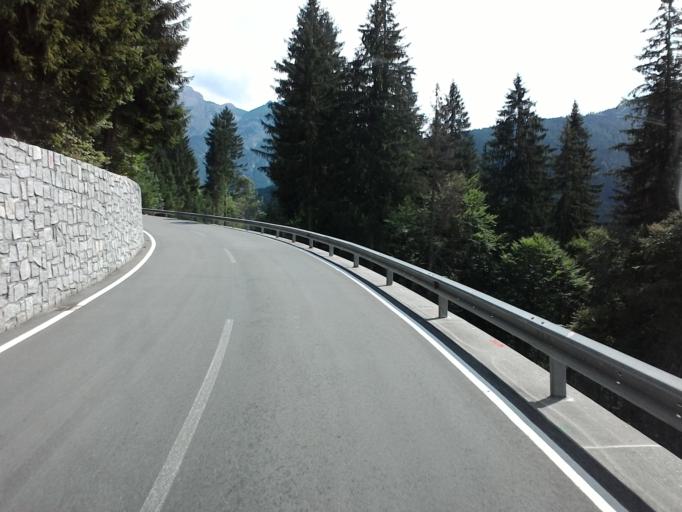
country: AT
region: Tyrol
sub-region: Politischer Bezirk Lienz
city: Nikolsdorf
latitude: 46.6871
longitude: 12.8588
